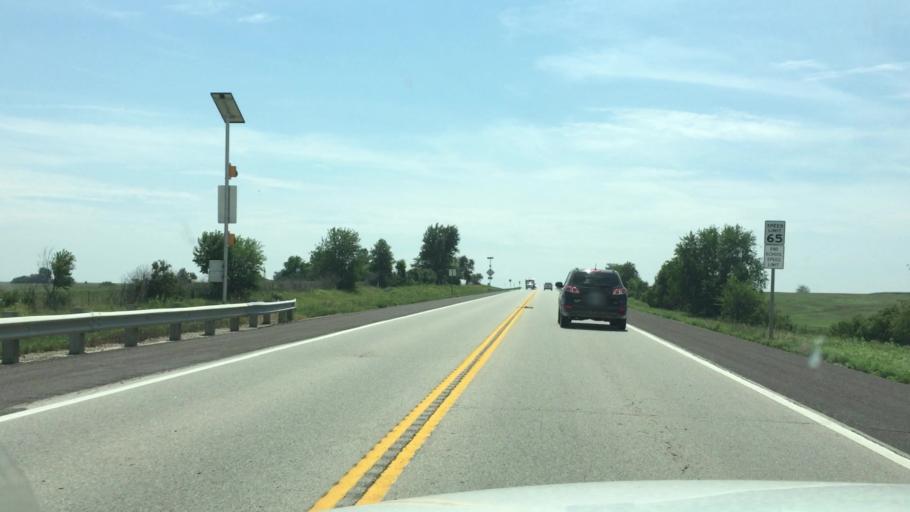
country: US
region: Kansas
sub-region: Jackson County
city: Holton
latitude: 39.5254
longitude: -95.7482
